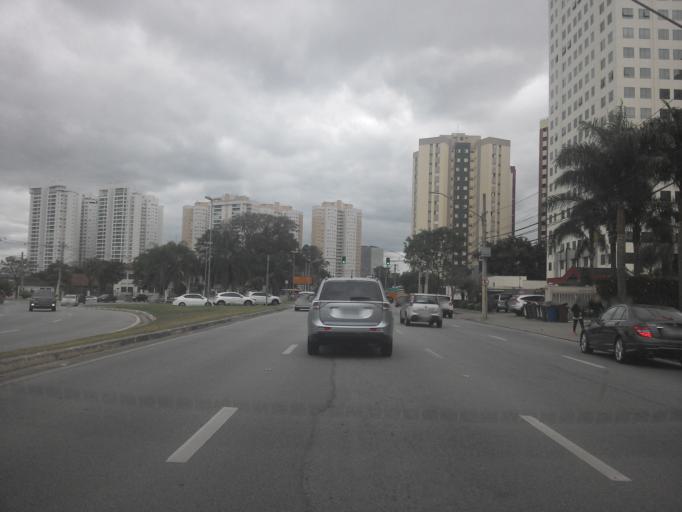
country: BR
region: Sao Paulo
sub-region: Sao Jose Dos Campos
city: Sao Jose dos Campos
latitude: -23.2130
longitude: -45.9096
